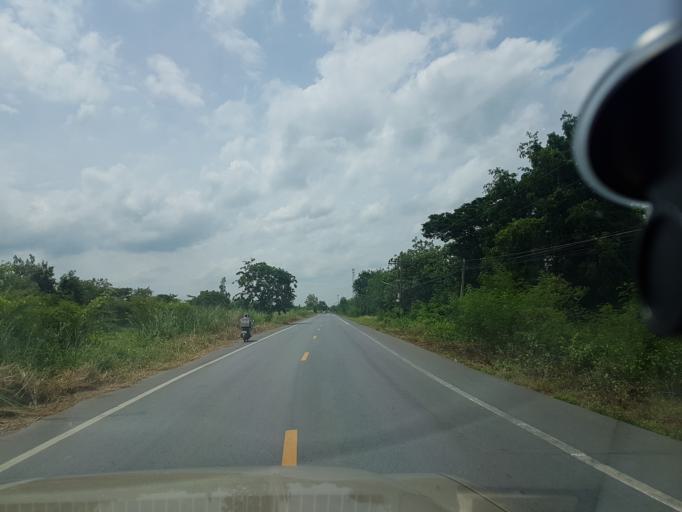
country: TH
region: Sara Buri
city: Nong Khae
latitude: 14.2363
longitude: 100.8919
